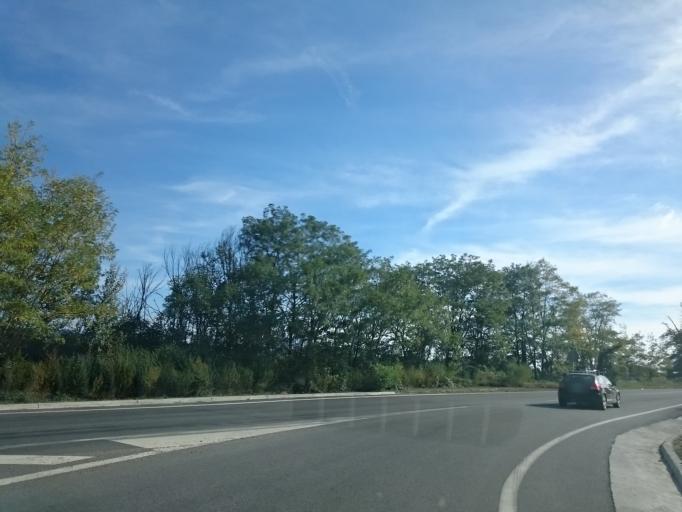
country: ES
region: Catalonia
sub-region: Provincia de Barcelona
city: Vic
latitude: 41.9490
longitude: 2.2745
